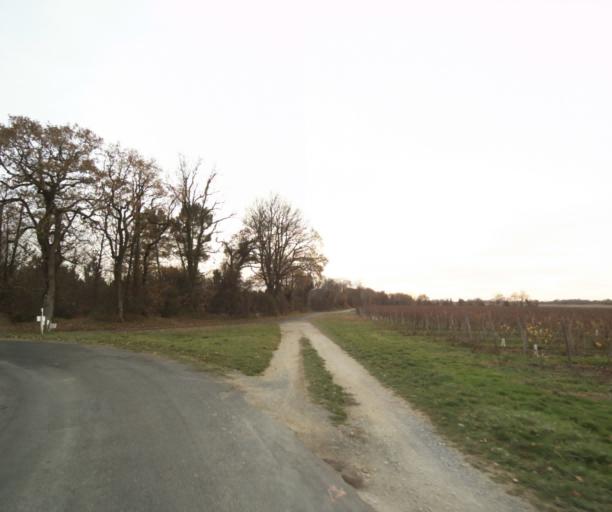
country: FR
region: Poitou-Charentes
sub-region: Departement de la Charente-Maritime
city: Fontcouverte
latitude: 45.7881
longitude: -0.5840
